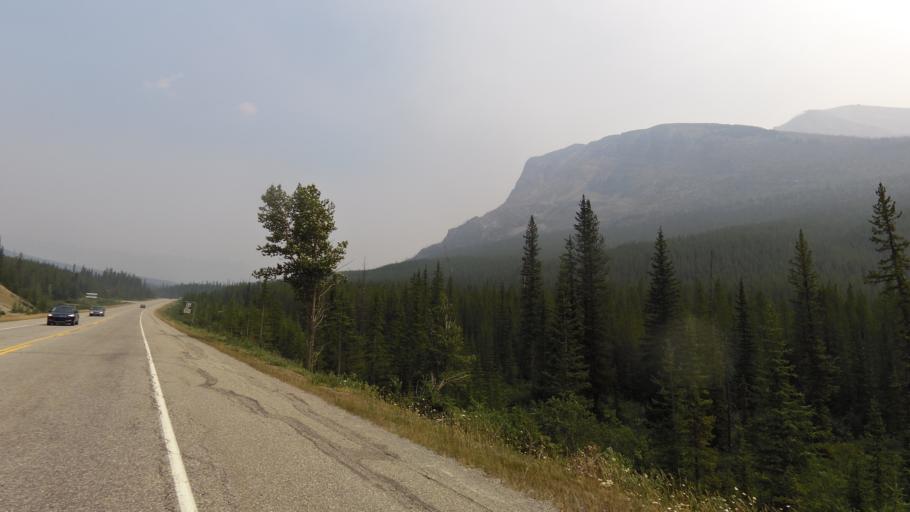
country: CA
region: Alberta
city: Lake Louise
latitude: 51.2232
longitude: -116.0575
